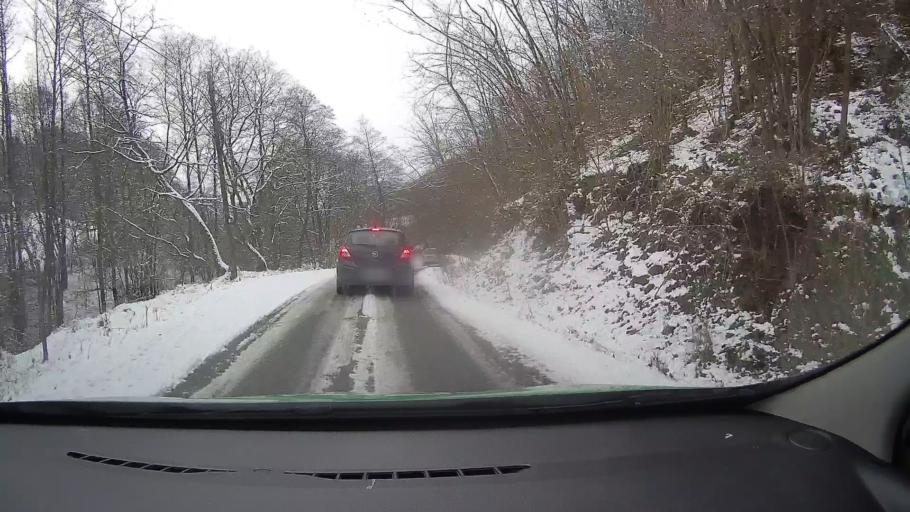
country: RO
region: Alba
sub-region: Comuna Almasu Mare
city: Almasu Mare
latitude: 46.0800
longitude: 23.1156
